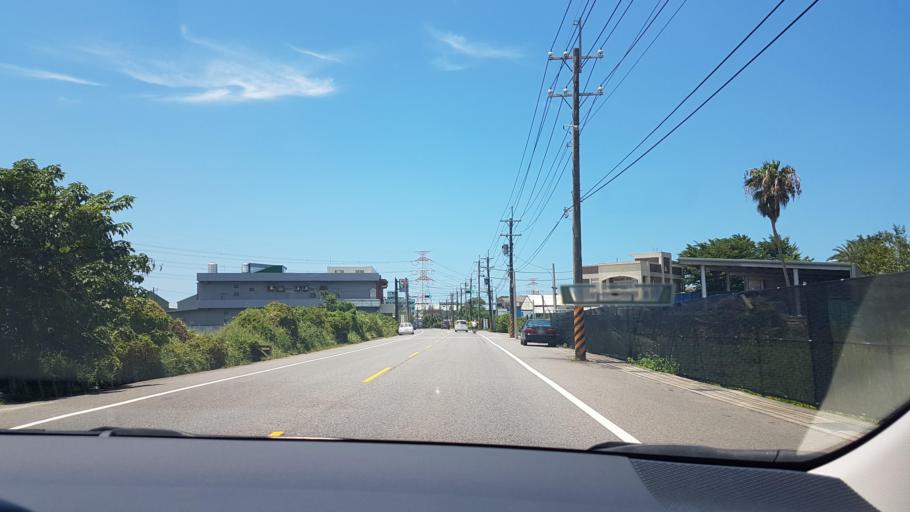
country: TW
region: Taiwan
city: Taoyuan City
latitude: 25.0888
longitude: 121.2778
